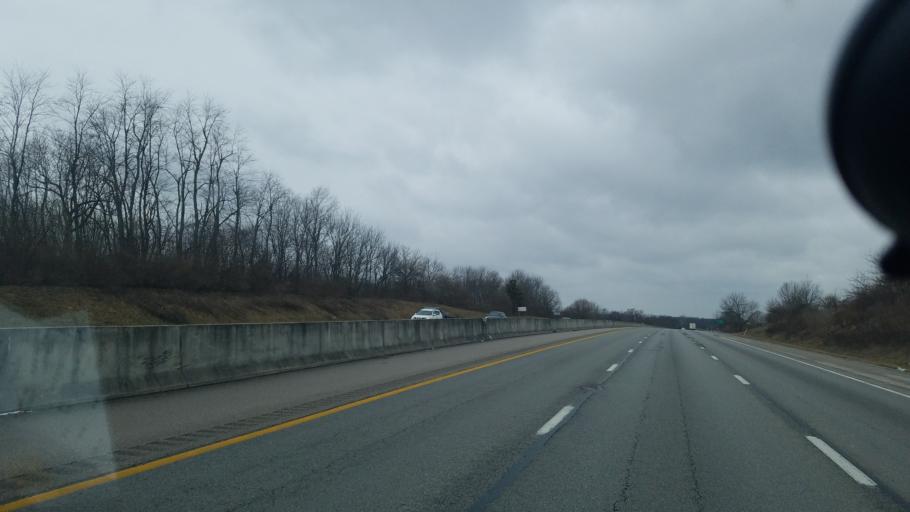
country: US
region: Kentucky
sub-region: Clark County
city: Winchester
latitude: 38.0367
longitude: -84.2861
